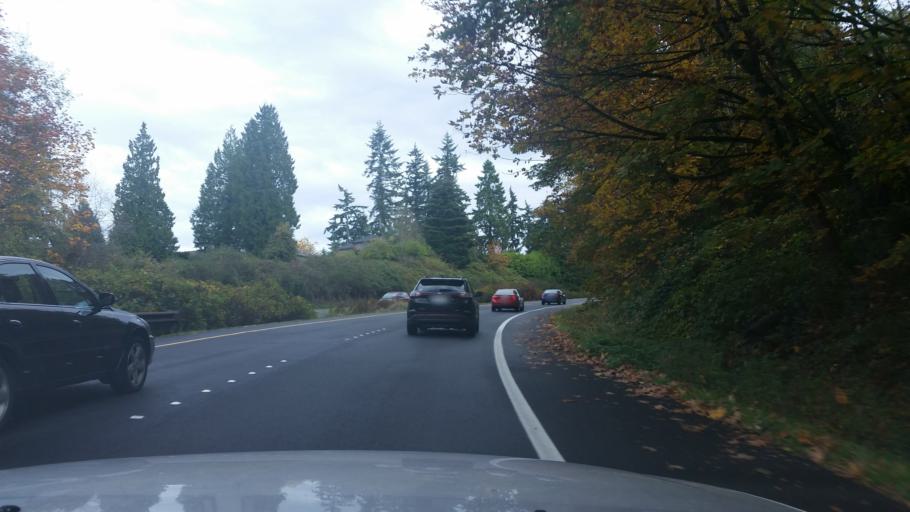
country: US
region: Washington
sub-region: King County
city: Eastgate
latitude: 47.6024
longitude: -122.1578
